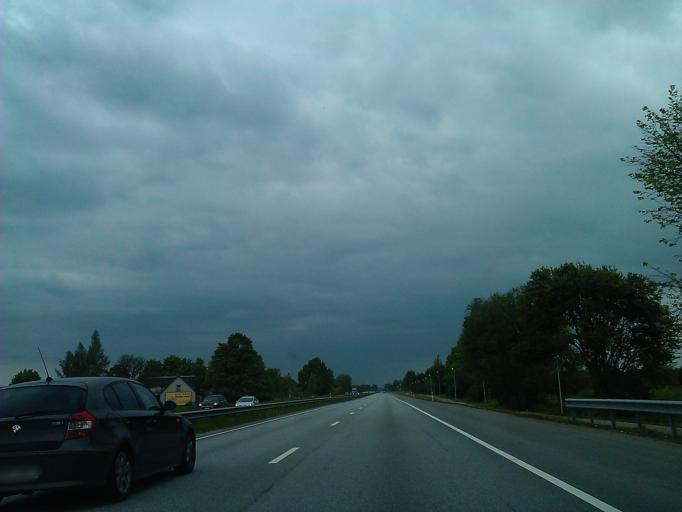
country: LV
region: Olaine
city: Olaine
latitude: 56.7978
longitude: 23.9760
